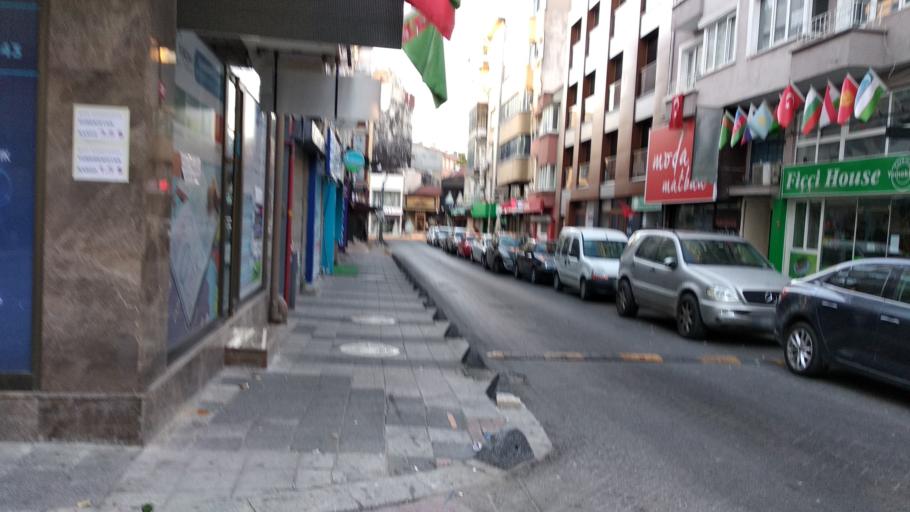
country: TR
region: Istanbul
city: UEskuedar
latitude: 40.9923
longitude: 29.0314
